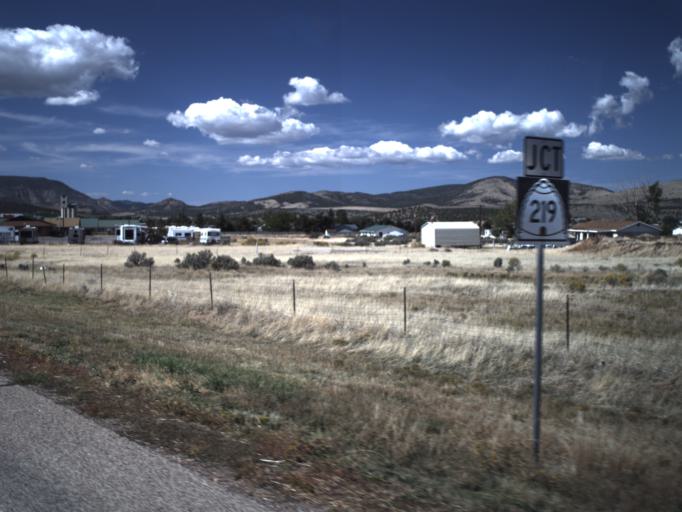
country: US
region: Utah
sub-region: Washington County
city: Enterprise
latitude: 37.5744
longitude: -113.7016
